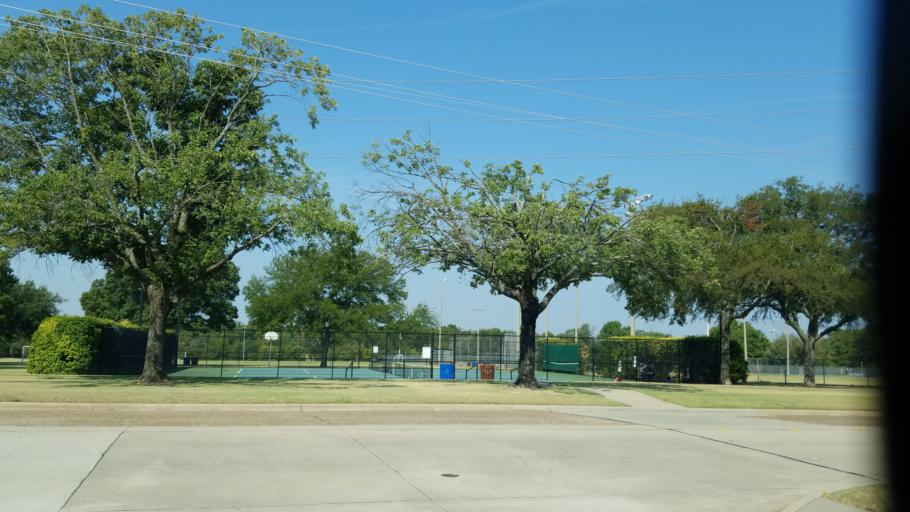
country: US
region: Texas
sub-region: Dallas County
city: Richardson
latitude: 32.9594
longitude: -96.7437
